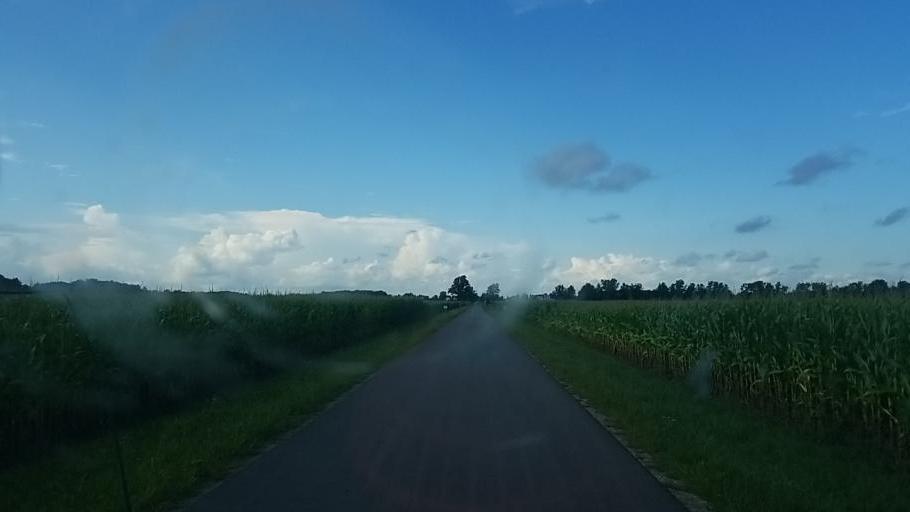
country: US
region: Ohio
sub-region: Hardin County
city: Forest
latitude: 40.7790
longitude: -83.4486
